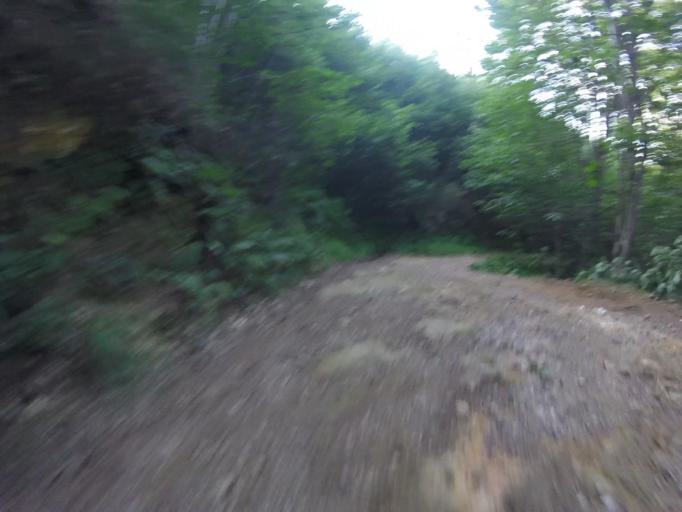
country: ES
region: Basque Country
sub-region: Provincia de Guipuzcoa
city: Irun
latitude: 43.3164
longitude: -1.7523
